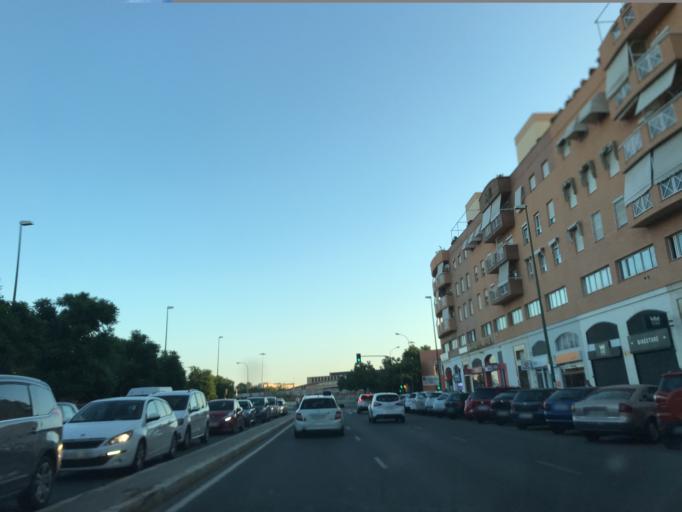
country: ES
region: Andalusia
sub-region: Provincia de Sevilla
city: Sevilla
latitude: 37.3876
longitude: -5.9778
